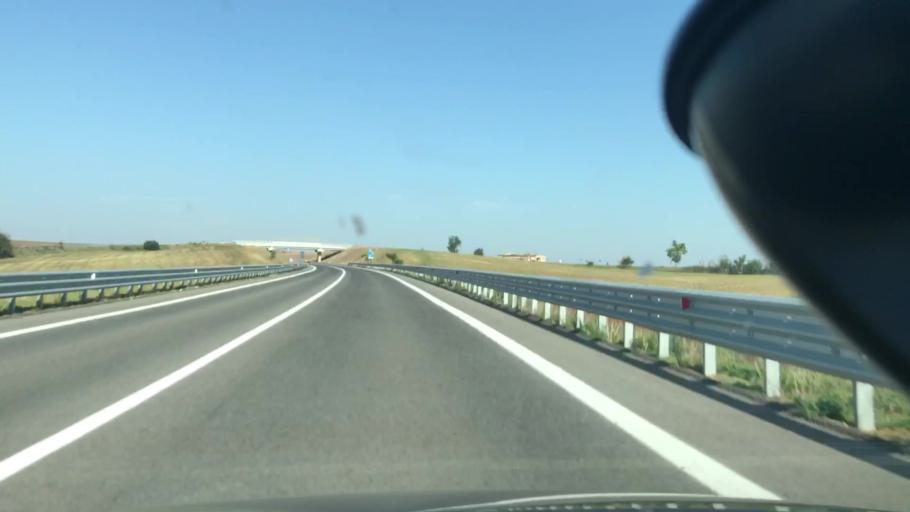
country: IT
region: Basilicate
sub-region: Provincia di Potenza
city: Palazzo San Gervasio
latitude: 40.9659
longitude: 16.0084
